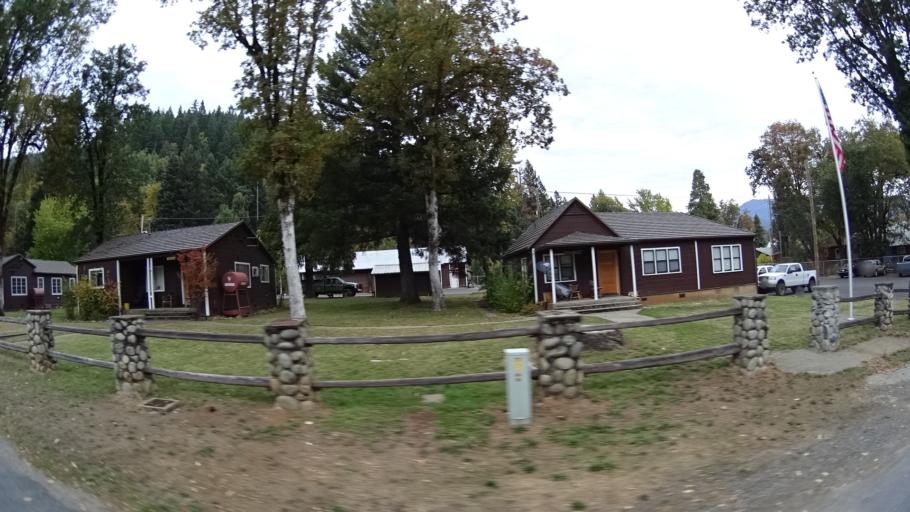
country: US
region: California
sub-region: Siskiyou County
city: Happy Camp
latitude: 41.7924
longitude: -123.3812
